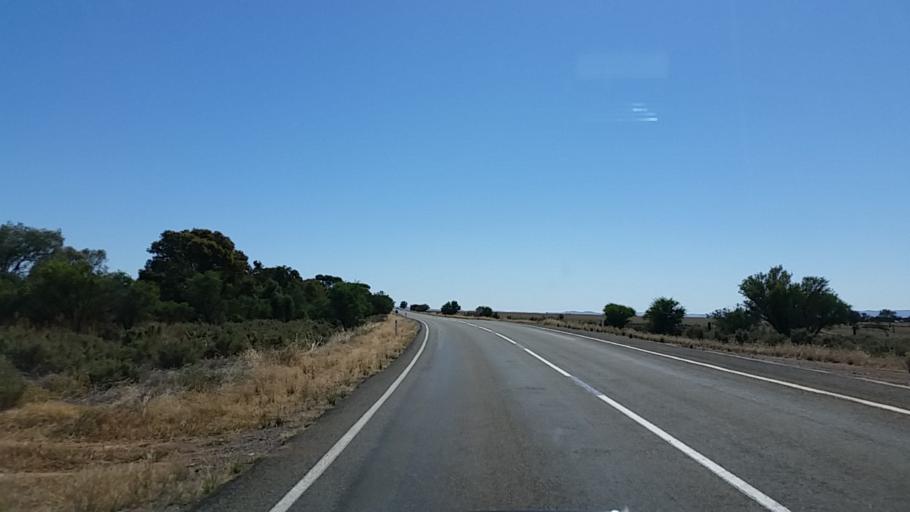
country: AU
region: South Australia
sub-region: Peterborough
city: Peterborough
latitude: -32.7637
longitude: 138.6555
